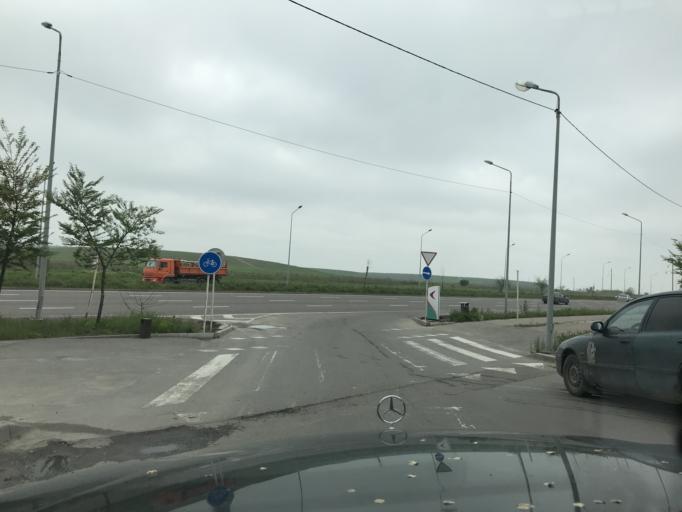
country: KZ
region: Almaty Oblysy
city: Burunday
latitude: 43.2957
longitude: 76.8330
